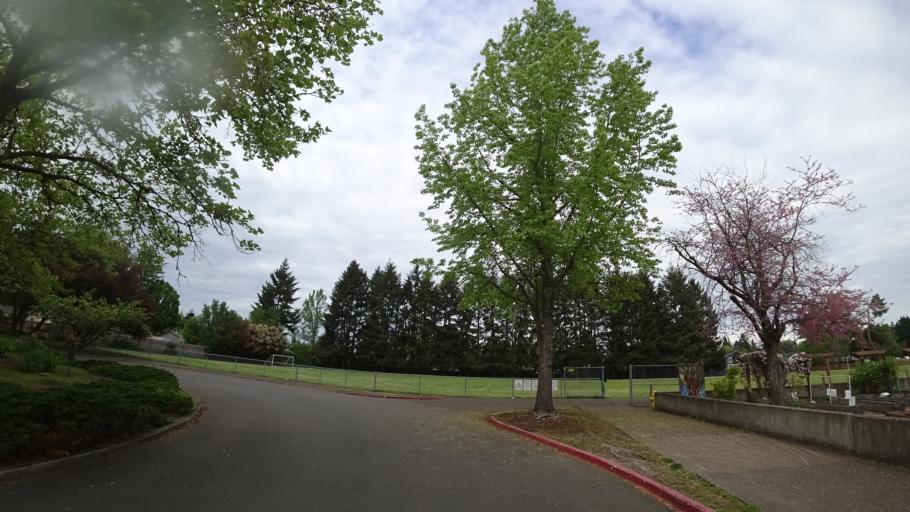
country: US
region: Oregon
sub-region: Washington County
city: Hillsboro
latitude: 45.4976
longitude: -122.9637
